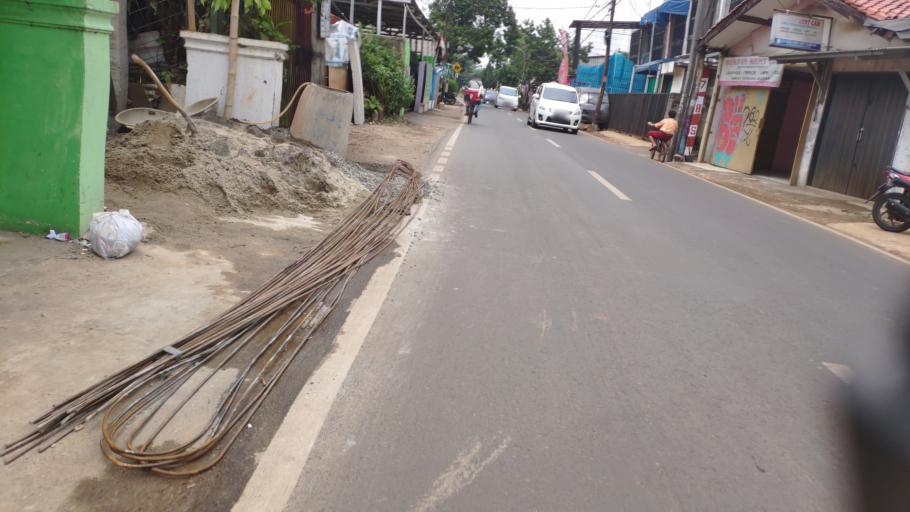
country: ID
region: West Java
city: Depok
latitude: -6.3476
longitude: 106.8206
